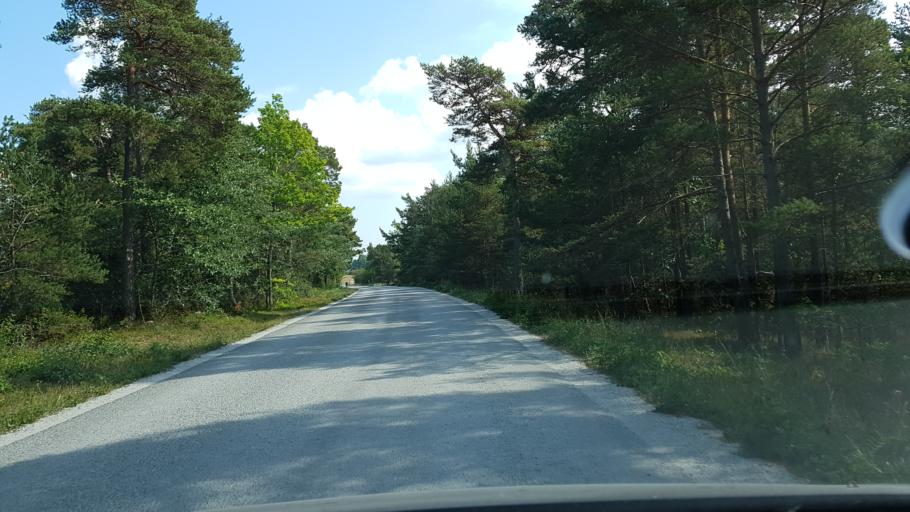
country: SE
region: Gotland
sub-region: Gotland
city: Visby
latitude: 57.8146
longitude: 18.5230
